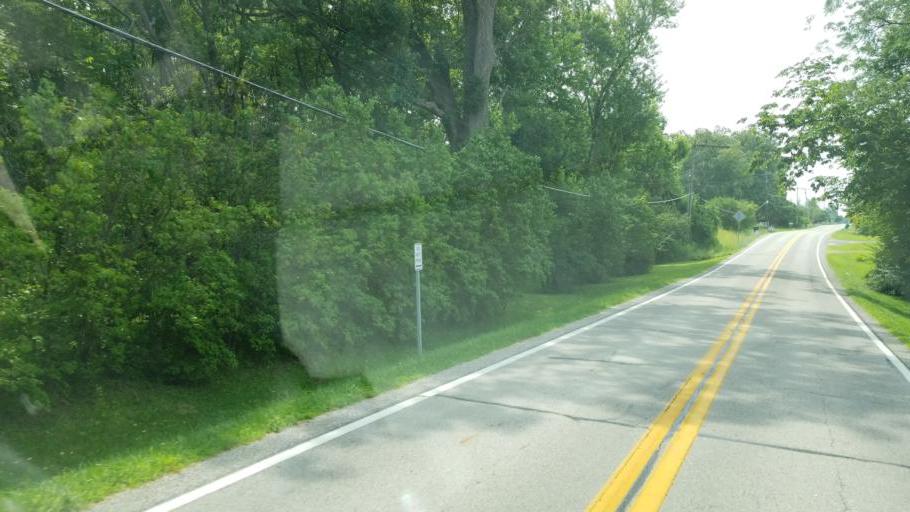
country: US
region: Ohio
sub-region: Madison County
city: West Jefferson
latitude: 39.9146
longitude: -83.2389
